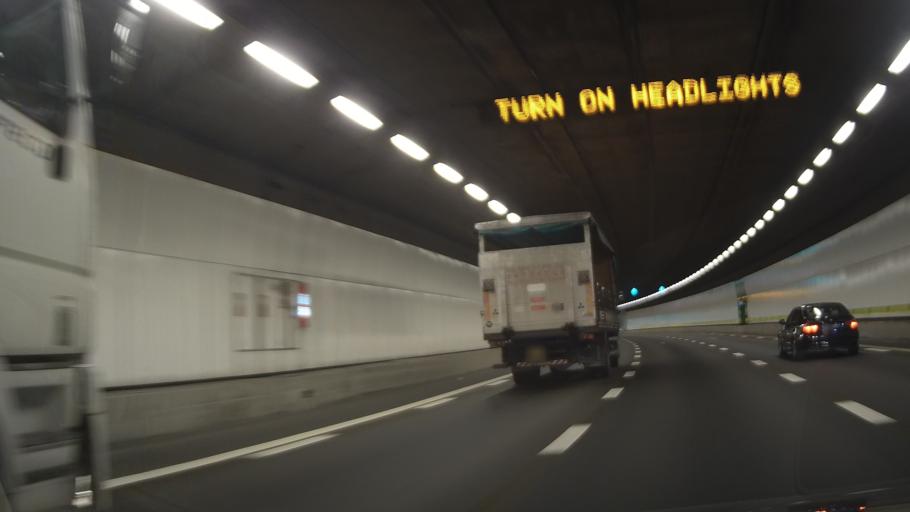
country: SG
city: Singapore
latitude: 1.3598
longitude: 103.9057
